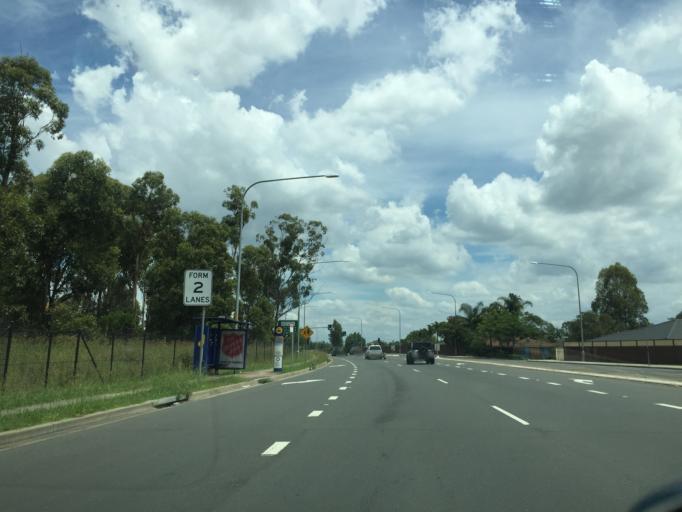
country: AU
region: New South Wales
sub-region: Blacktown
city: Hassall Grove
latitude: -33.7343
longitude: 150.8469
